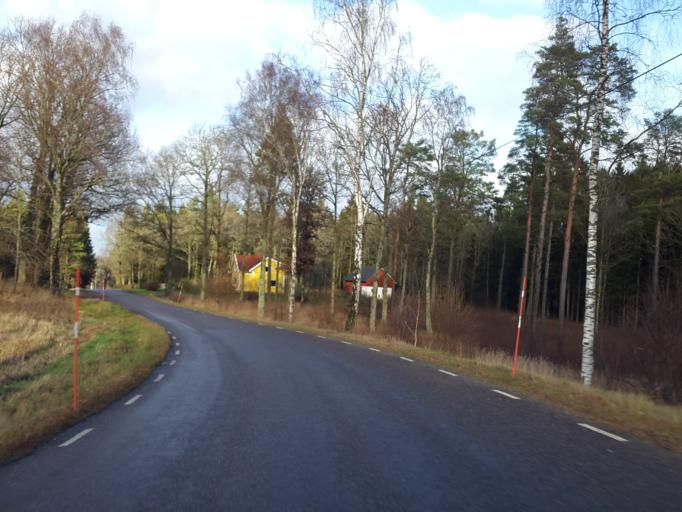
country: SE
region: Vaestra Goetaland
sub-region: Vargarda Kommun
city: Jonstorp
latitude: 58.0010
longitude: 12.7601
